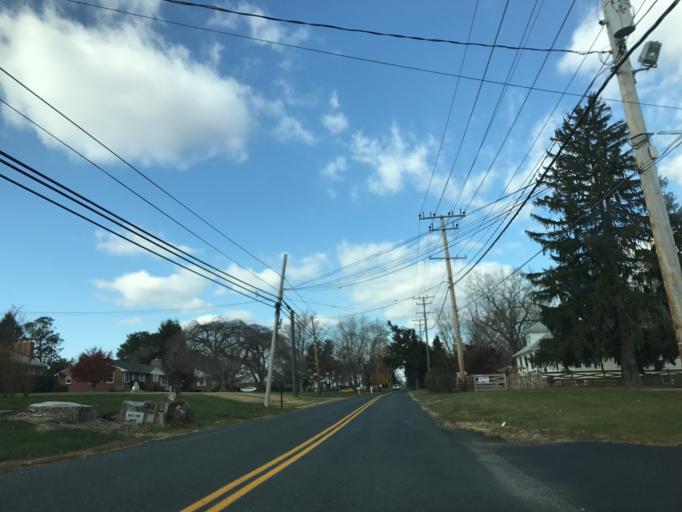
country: US
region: Maryland
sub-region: Harford County
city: Fallston
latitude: 39.5073
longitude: -76.4053
